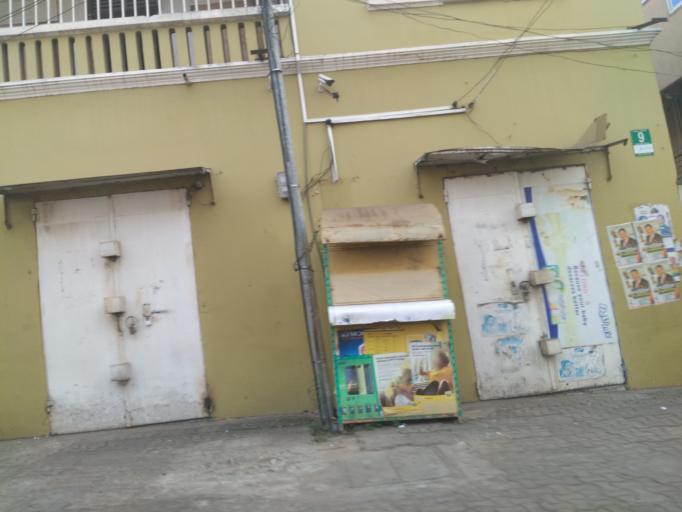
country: GH
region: Ashanti
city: Kumasi
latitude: 6.6960
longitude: -1.6239
